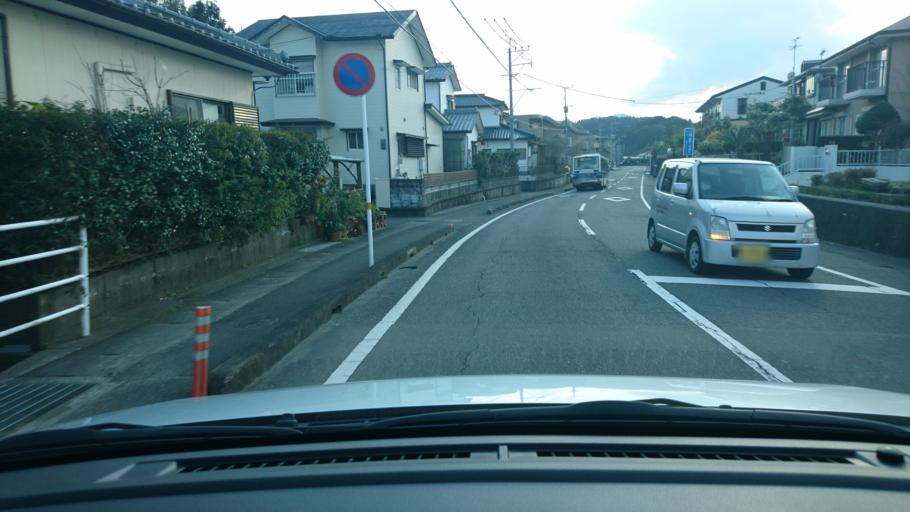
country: JP
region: Miyazaki
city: Miyazaki-shi
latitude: 31.8721
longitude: 131.4054
